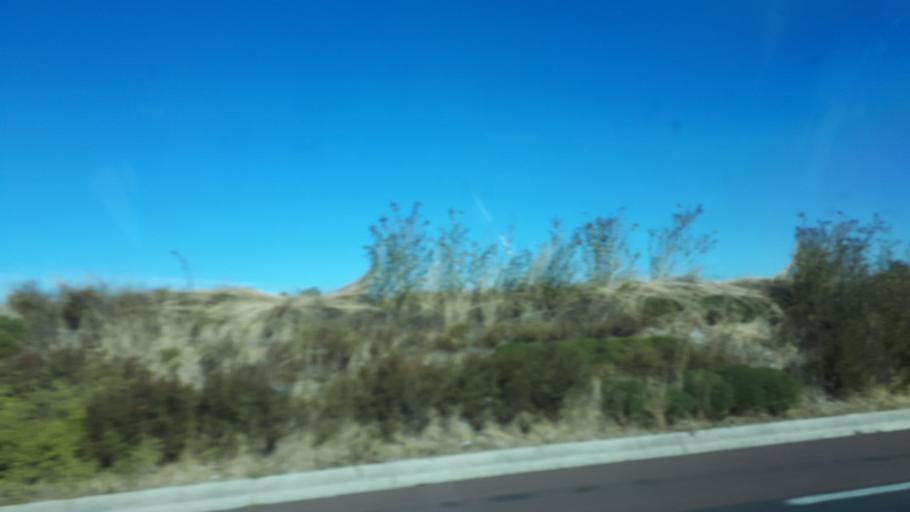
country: FR
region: Centre
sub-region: Departement d'Eure-et-Loir
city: Chateaudun
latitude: 48.0609
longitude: 1.3477
